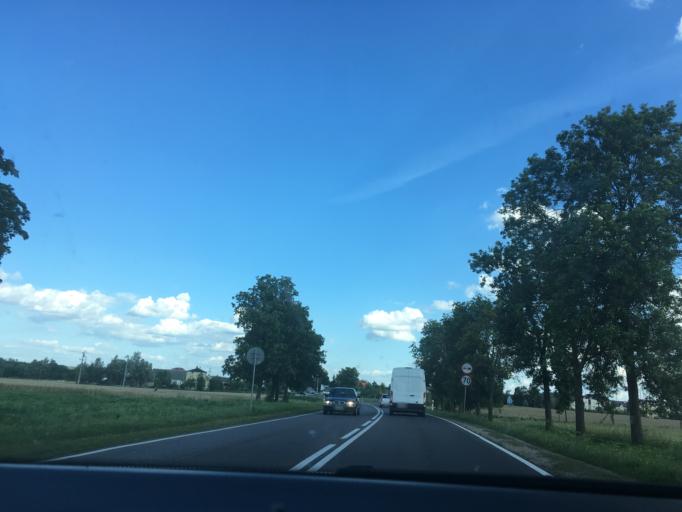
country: PL
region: Podlasie
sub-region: Powiat bialostocki
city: Zabludow
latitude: 53.0204
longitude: 23.3225
